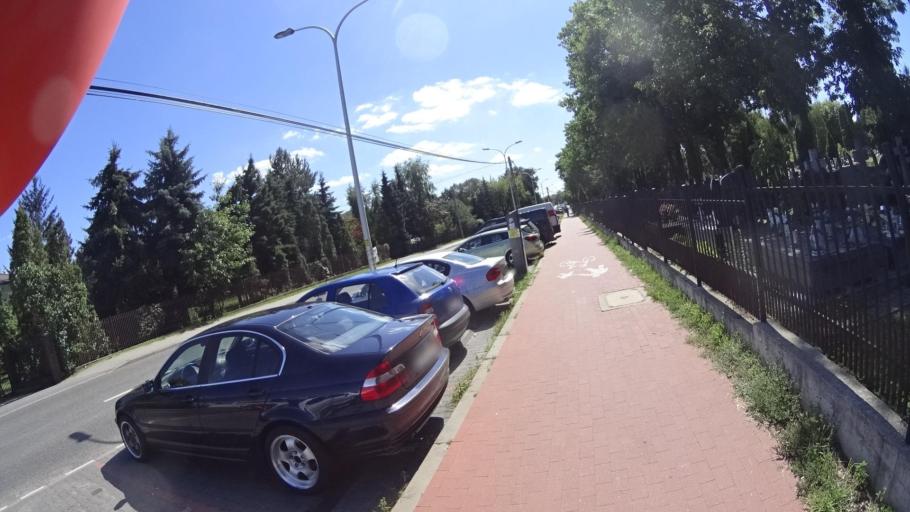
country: PL
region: Masovian Voivodeship
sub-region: Powiat piaseczynski
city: Jozefoslaw
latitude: 52.0832
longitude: 21.0427
